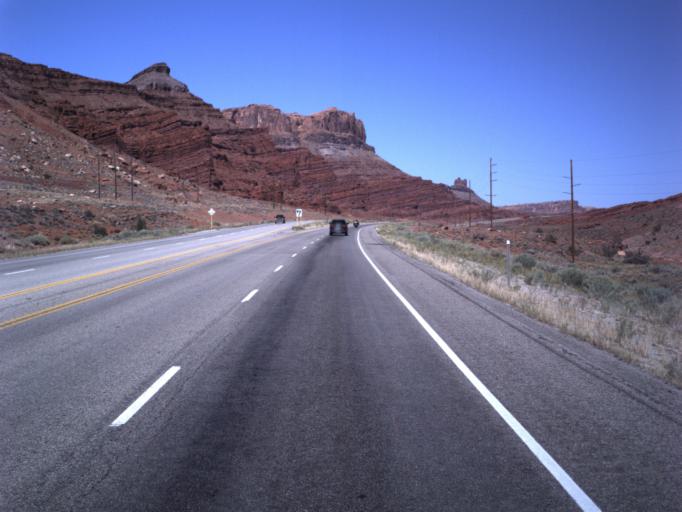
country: US
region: Utah
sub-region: Grand County
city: Moab
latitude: 38.6207
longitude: -109.6413
